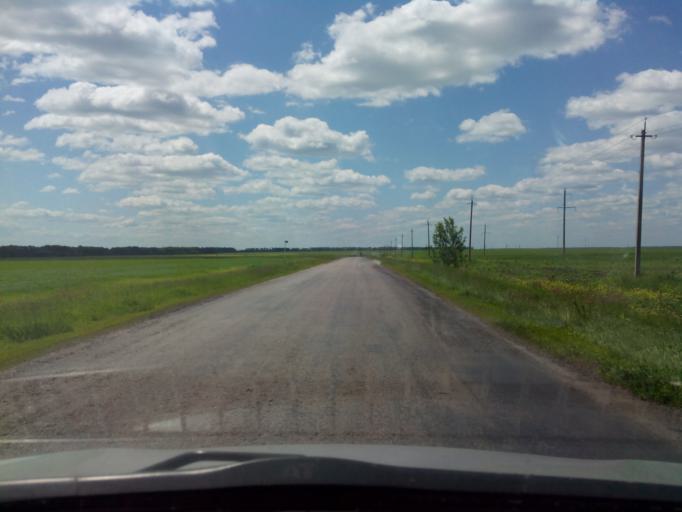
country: RU
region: Voronezj
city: Gribanovskiy
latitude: 51.6057
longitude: 41.8522
